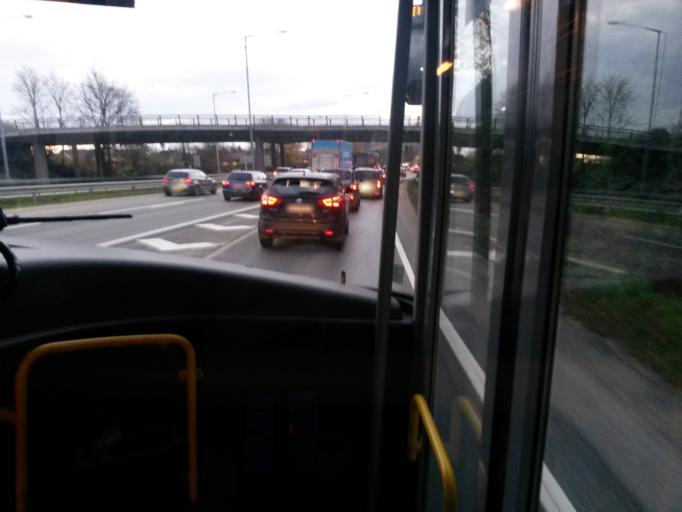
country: NO
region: Rogaland
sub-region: Stavanger
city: Stavanger
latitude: 58.9422
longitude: 5.7252
